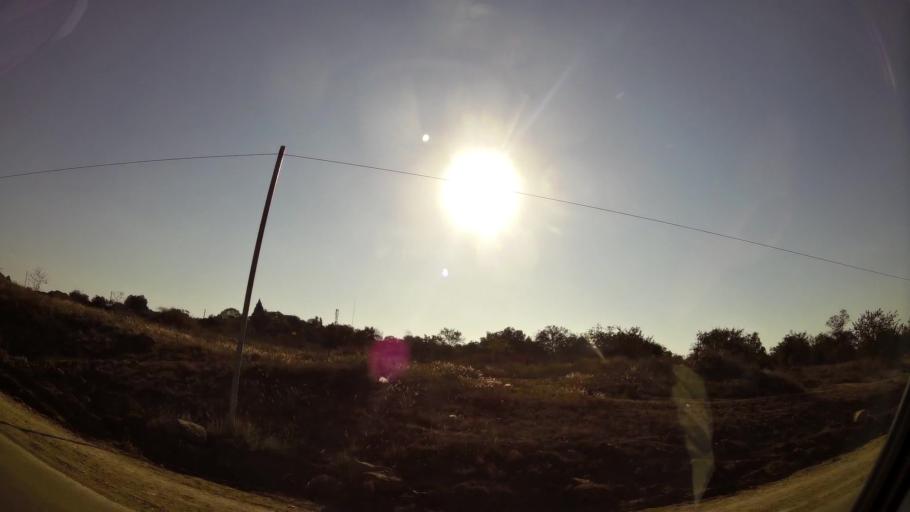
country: ZA
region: Gauteng
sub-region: City of Tshwane Metropolitan Municipality
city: Pretoria
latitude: -25.7696
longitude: 28.3548
